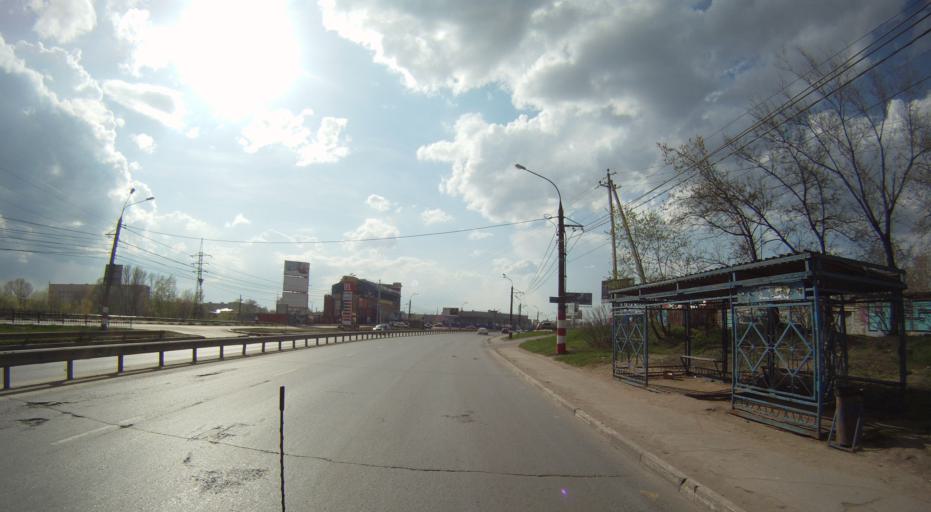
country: RU
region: Nizjnij Novgorod
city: Nizhniy Novgorod
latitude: 56.2963
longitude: 43.9323
